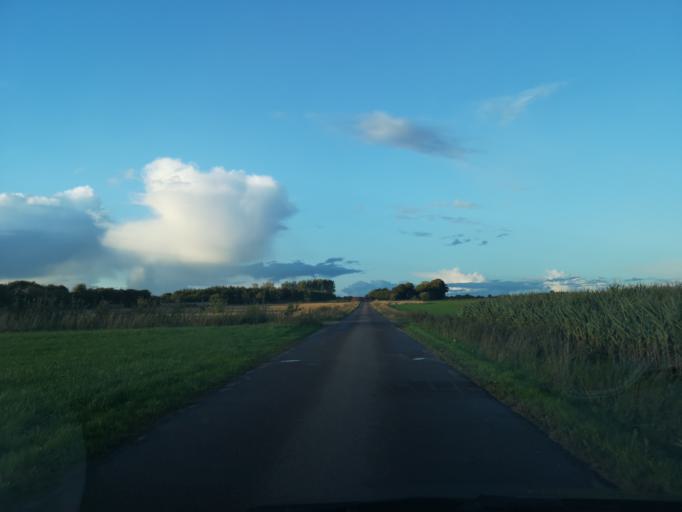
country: DK
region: Central Jutland
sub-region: Ringkobing-Skjern Kommune
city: Skjern
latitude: 56.0226
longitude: 8.5577
